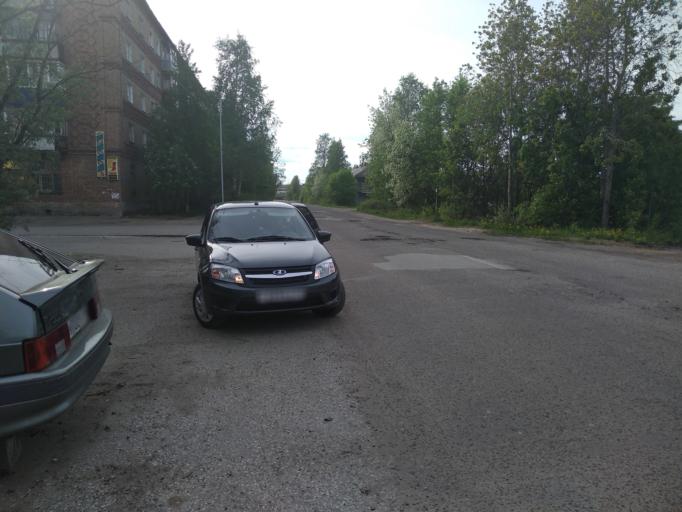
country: RU
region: Komi Republic
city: Pechora
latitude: 65.1466
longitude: 57.2208
